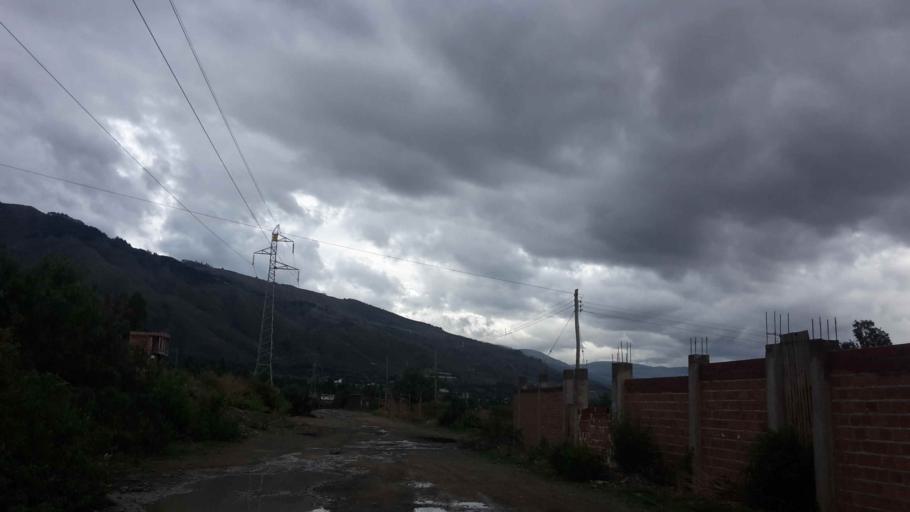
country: BO
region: Cochabamba
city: Cochabamba
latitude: -17.3781
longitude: -66.0613
